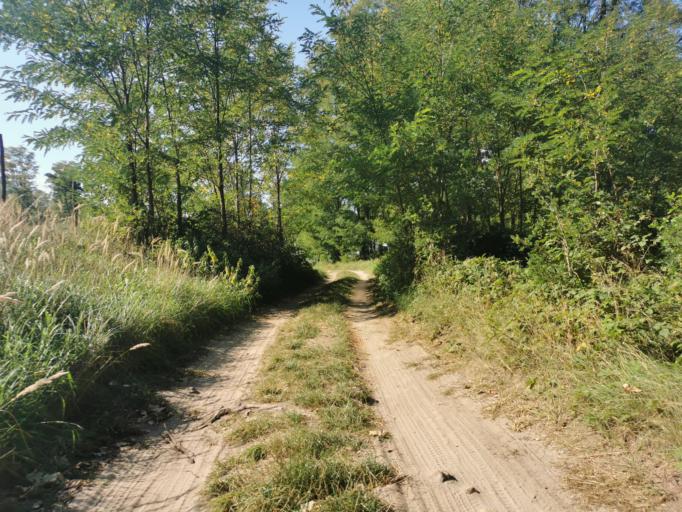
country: SK
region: Trnavsky
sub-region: Okres Senica
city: Senica
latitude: 48.5990
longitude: 17.2470
